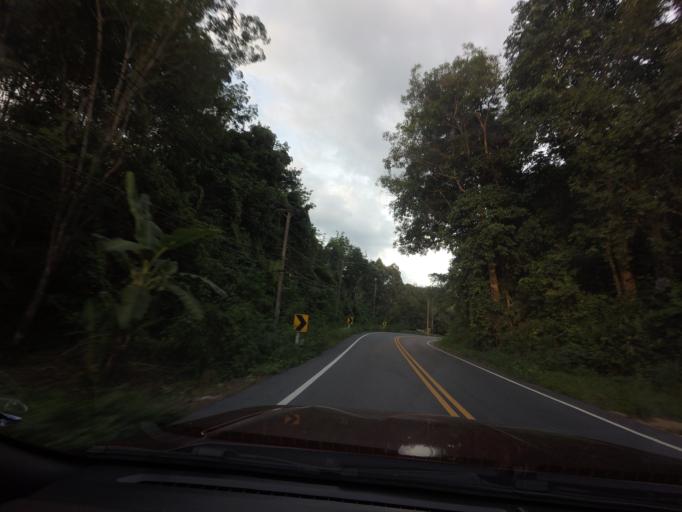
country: TH
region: Yala
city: Than To
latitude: 6.0372
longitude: 101.2042
